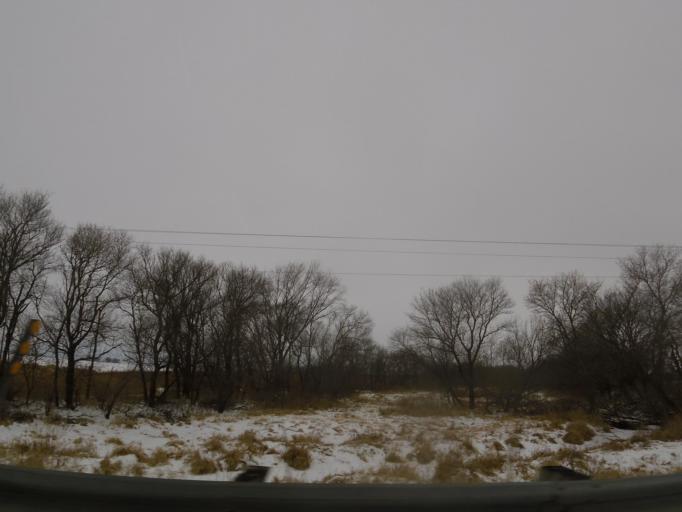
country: US
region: Iowa
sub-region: Bremer County
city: Tripoli
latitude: 42.8266
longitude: -92.3375
